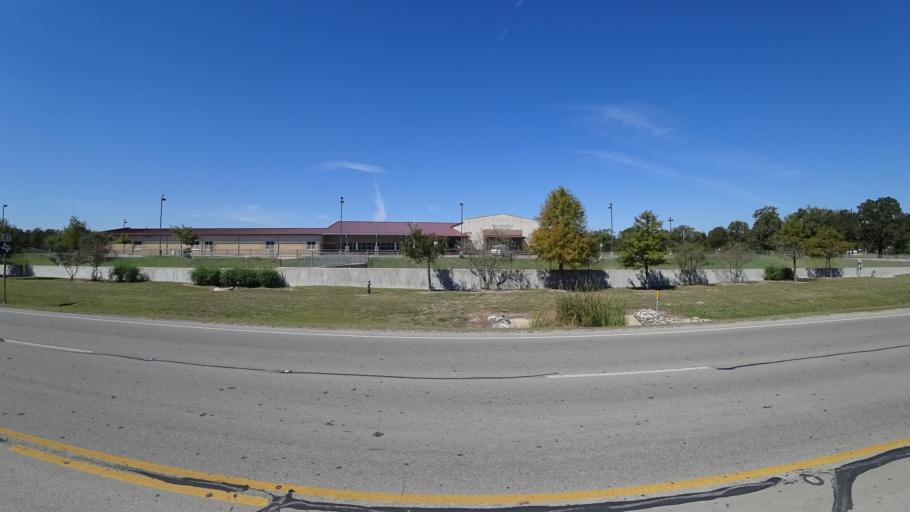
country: US
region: Texas
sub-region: Travis County
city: Hornsby Bend
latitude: 30.2805
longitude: -97.6349
